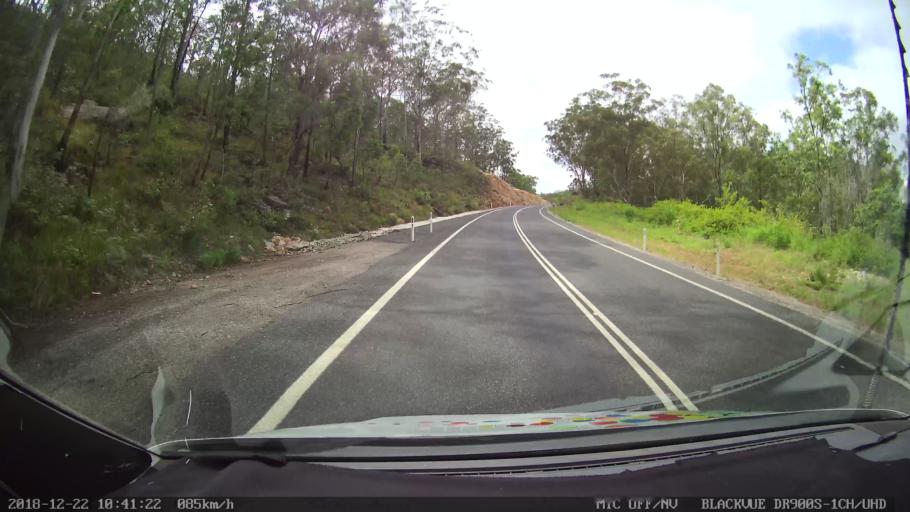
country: AU
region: New South Wales
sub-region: Clarence Valley
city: South Grafton
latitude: -29.6318
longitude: 152.7616
